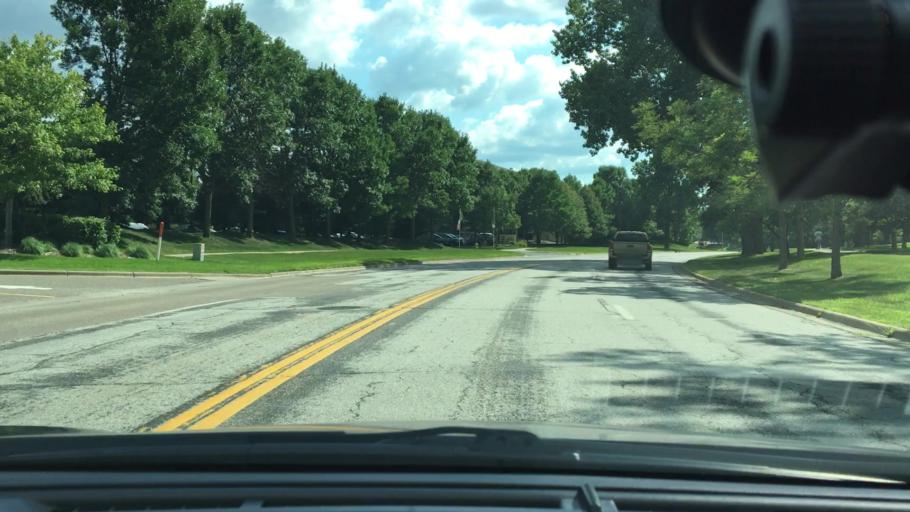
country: US
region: Minnesota
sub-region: Hennepin County
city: New Hope
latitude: 45.0387
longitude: -93.4054
